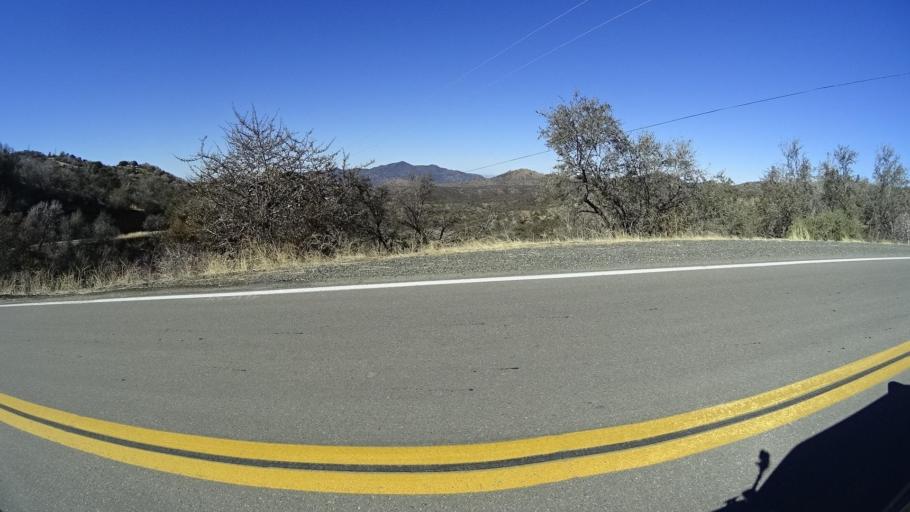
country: US
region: California
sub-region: Kern County
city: Alta Sierra
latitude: 35.7379
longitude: -118.6418
